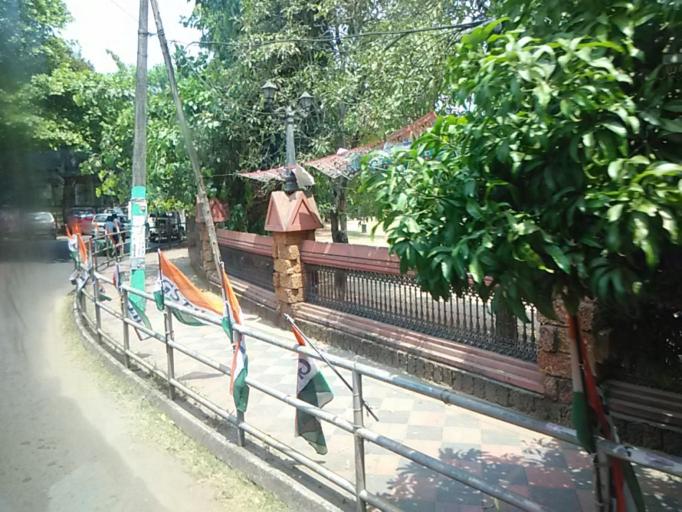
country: IN
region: Kerala
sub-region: Kozhikode
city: Kozhikode
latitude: 11.2527
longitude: 75.7812
